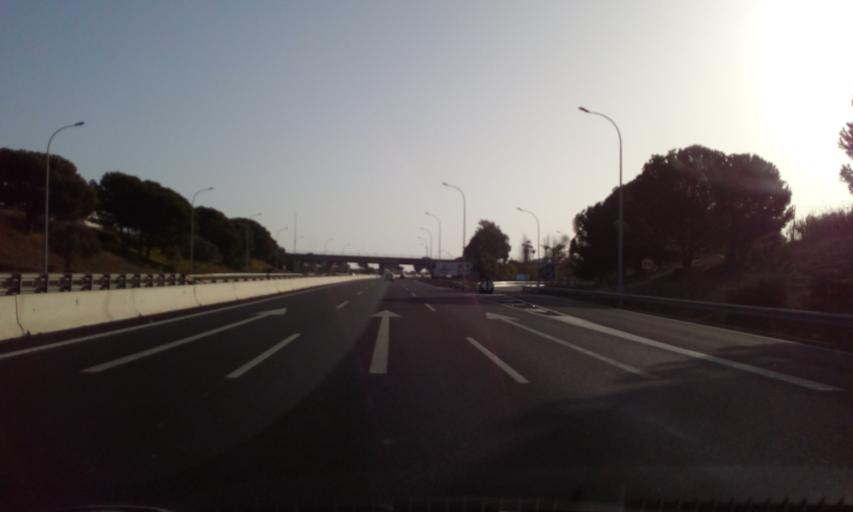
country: ES
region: Andalusia
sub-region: Provincia de Sevilla
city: Benacazon
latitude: 37.3616
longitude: -6.2030
